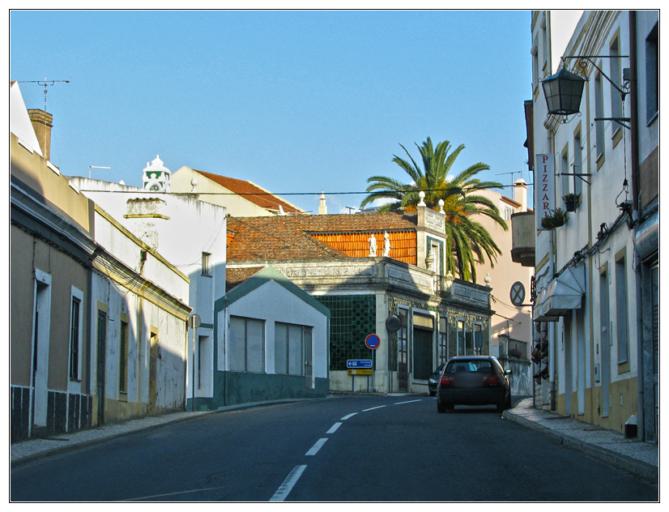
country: PT
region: Setubal
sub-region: Santiago do Cacem
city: Cercal
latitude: 37.8025
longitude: -8.6745
